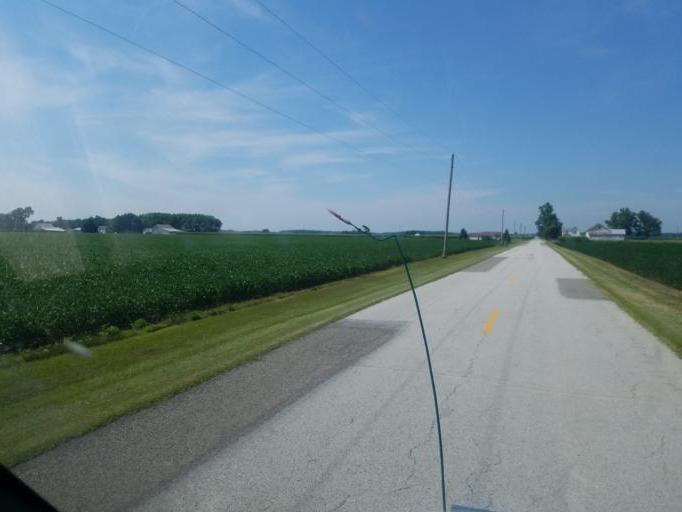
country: US
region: Ohio
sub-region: Shelby County
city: Jackson Center
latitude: 40.5305
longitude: -84.0120
